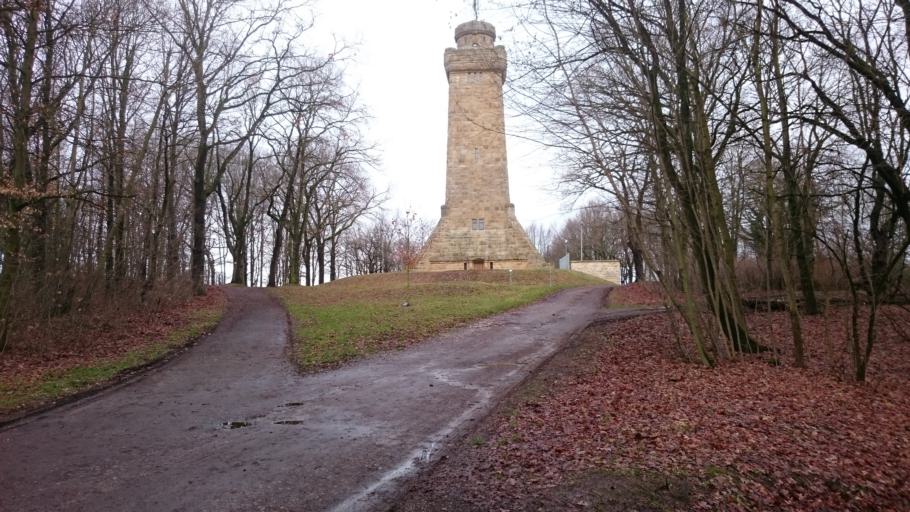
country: DE
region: Saxony
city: Glauchau
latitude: 50.8076
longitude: 12.5645
